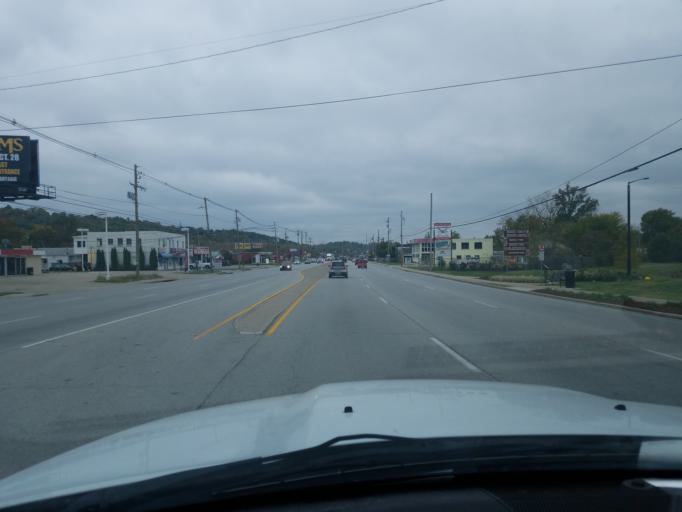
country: US
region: Kentucky
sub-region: Jefferson County
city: Pleasure Ridge Park
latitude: 38.1460
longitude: -85.8385
